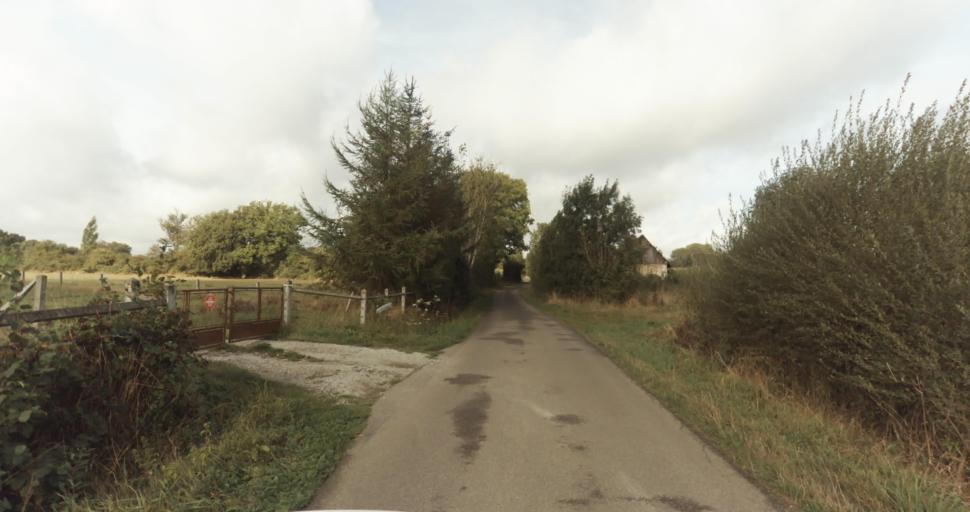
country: FR
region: Lower Normandy
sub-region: Departement de l'Orne
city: Gace
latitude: 48.8547
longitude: 0.3569
